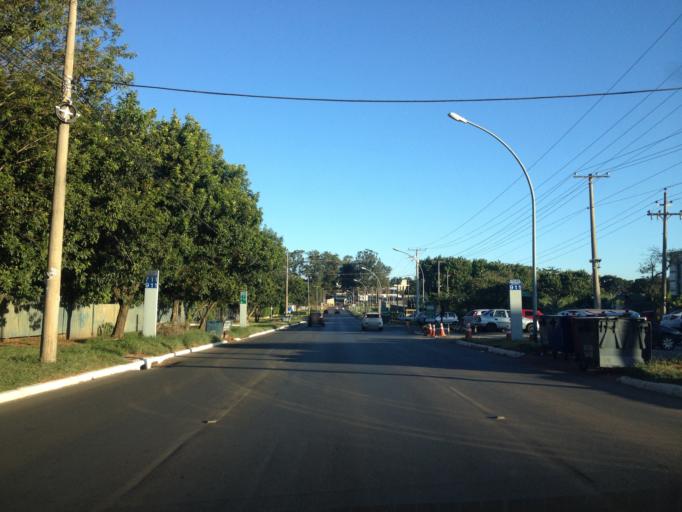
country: BR
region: Federal District
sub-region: Brasilia
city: Brasilia
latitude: -15.7551
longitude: -47.8983
